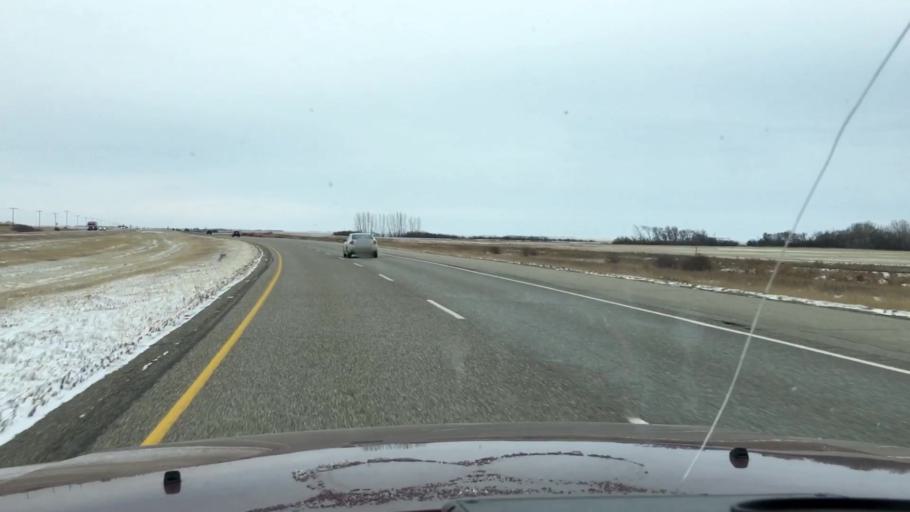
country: CA
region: Saskatchewan
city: Watrous
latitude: 51.1440
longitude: -105.9060
